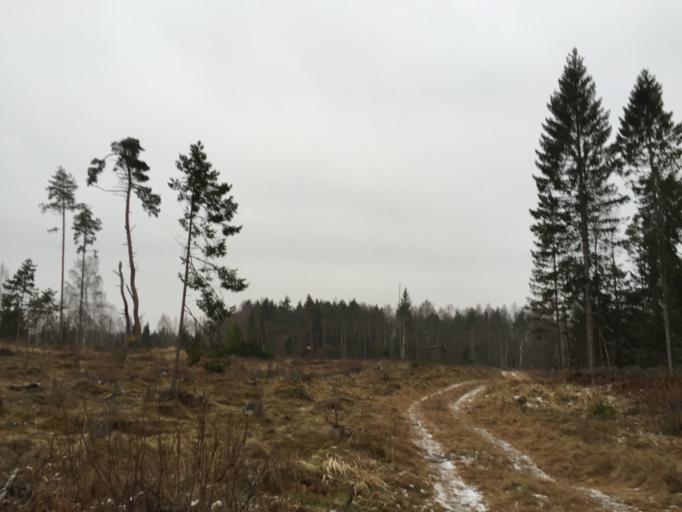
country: EE
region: Saare
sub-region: Kuressaare linn
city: Kuressaare
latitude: 58.4986
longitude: 22.3770
